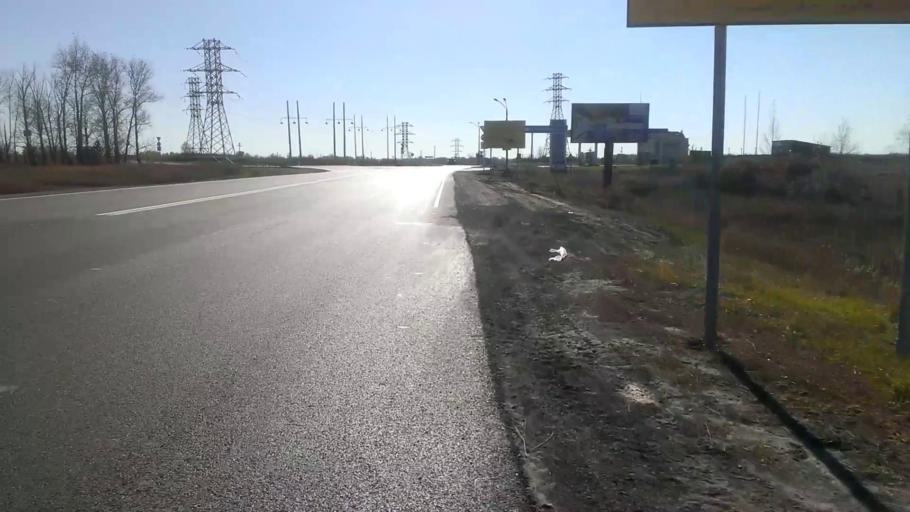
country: RU
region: Altai Krai
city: Sannikovo
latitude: 53.3378
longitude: 83.9385
